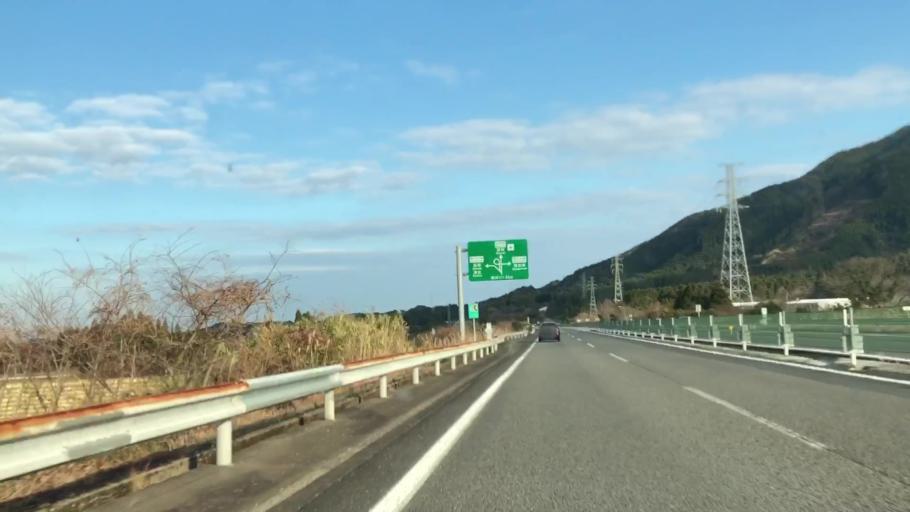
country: JP
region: Miyazaki
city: Miyazaki-shi
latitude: 31.8328
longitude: 131.3288
